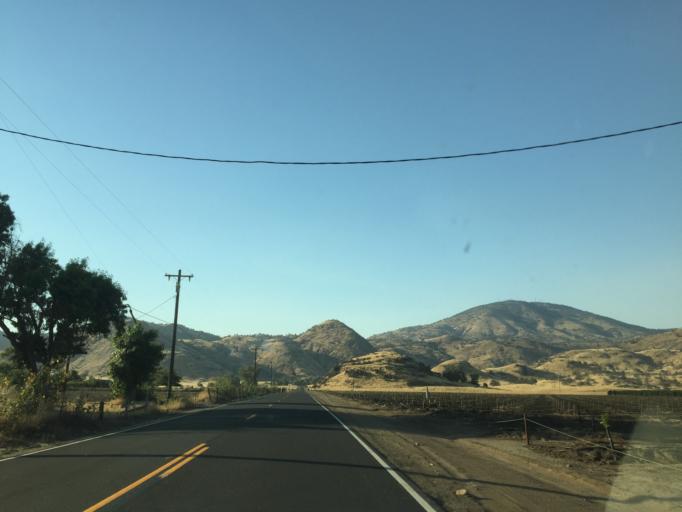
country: US
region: California
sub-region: Fresno County
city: Squaw Valley
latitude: 36.6974
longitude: -119.3044
